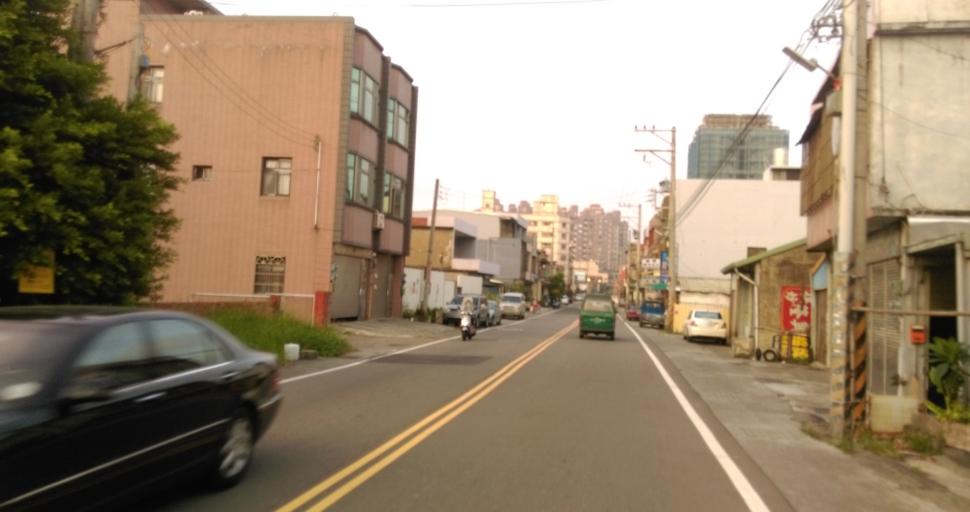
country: TW
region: Taiwan
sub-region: Hsinchu
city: Hsinchu
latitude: 24.8351
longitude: 120.9303
